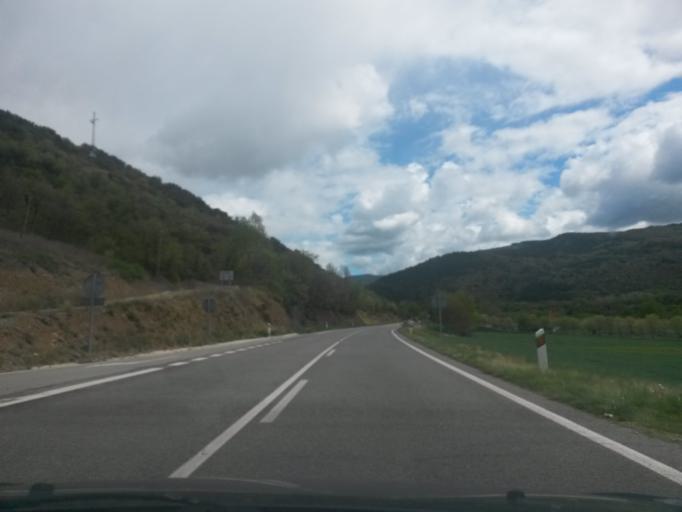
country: ES
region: Catalonia
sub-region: Provincia de Lleida
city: Alas i Cerc
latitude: 42.3581
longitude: 1.4993
